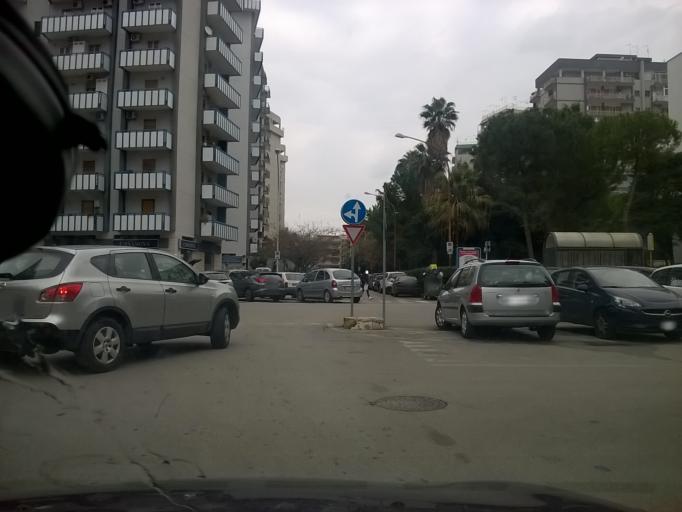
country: IT
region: Apulia
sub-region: Provincia di Taranto
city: Taranto
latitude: 40.4560
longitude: 17.2555
